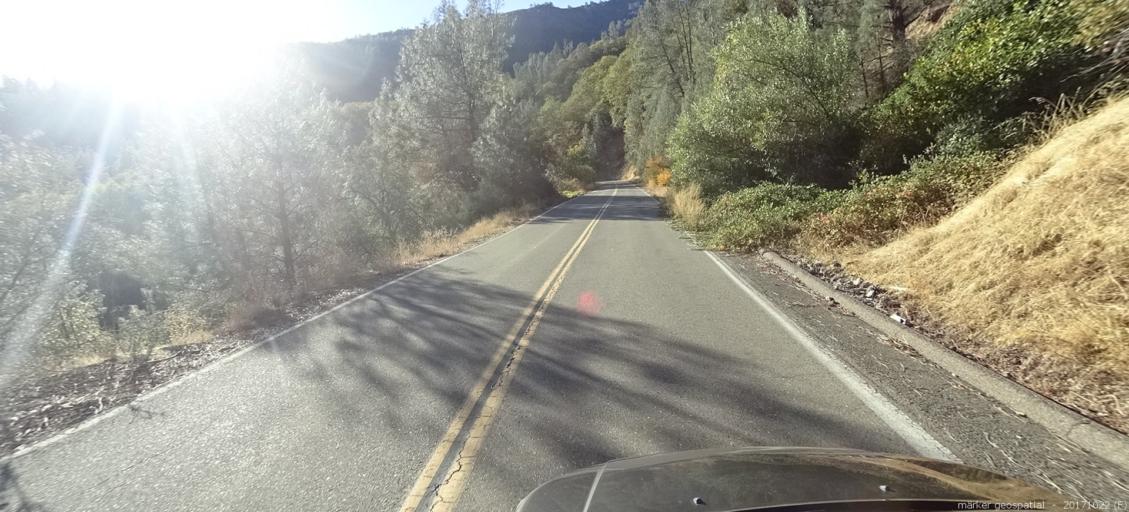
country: US
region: California
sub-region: Shasta County
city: Bella Vista
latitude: 40.8869
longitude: -122.2286
